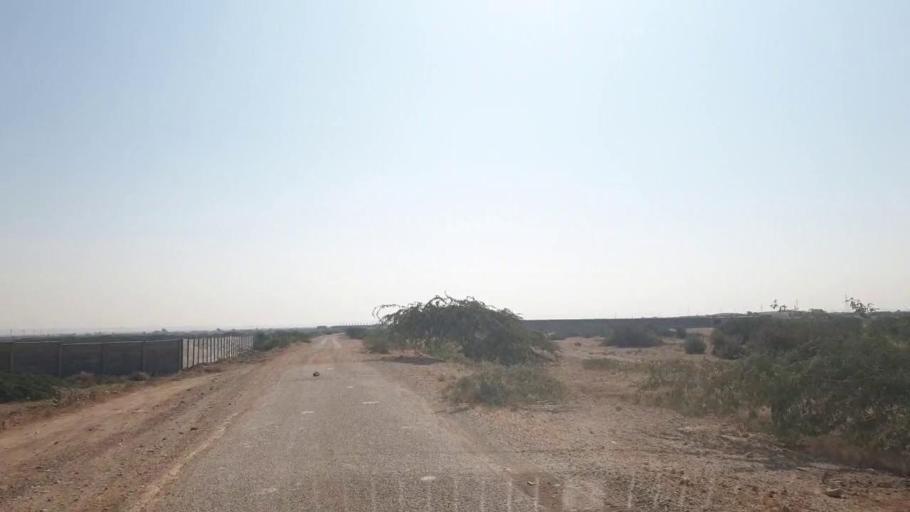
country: PK
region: Sindh
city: Gharo
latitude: 25.1475
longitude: 67.7243
